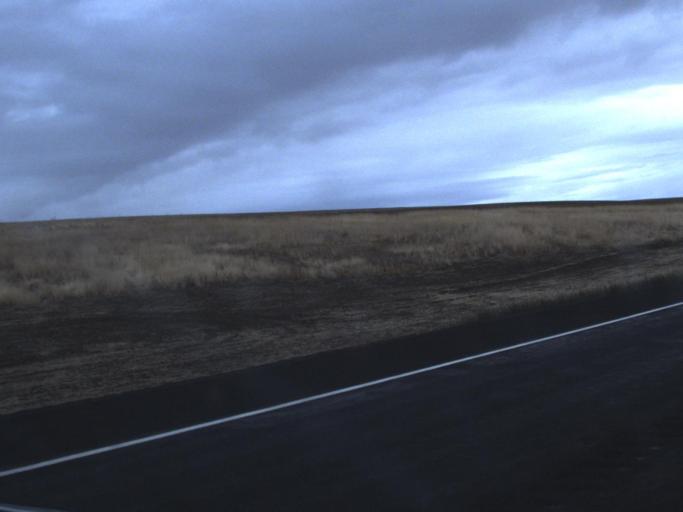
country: US
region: Washington
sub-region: Whitman County
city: Pullman
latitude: 46.5825
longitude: -117.1556
